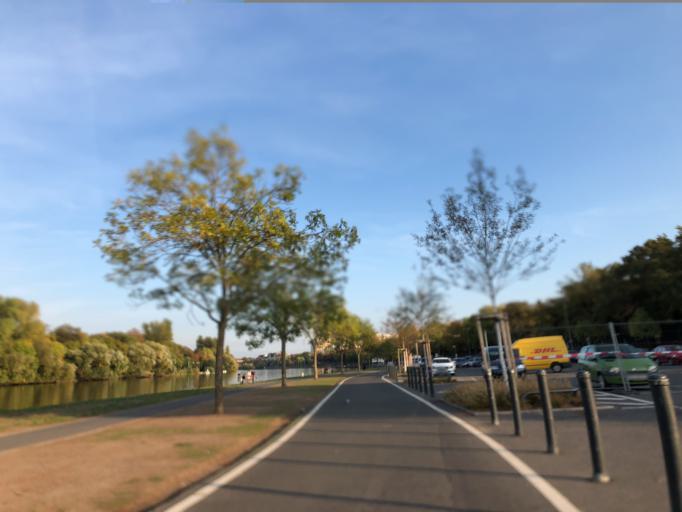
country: DE
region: Hesse
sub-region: Regierungsbezirk Darmstadt
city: Offenbach
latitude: 50.1103
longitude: 8.7601
